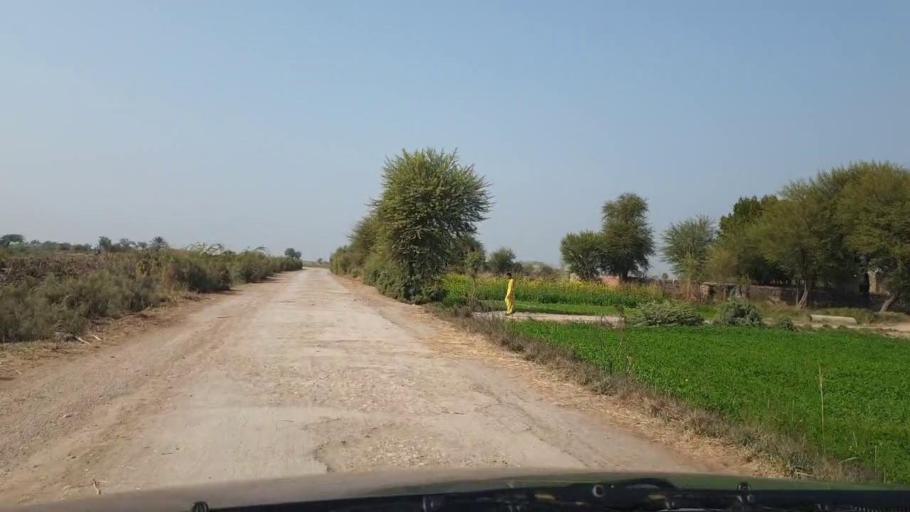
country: PK
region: Sindh
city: Sanghar
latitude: 26.0163
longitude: 68.9212
